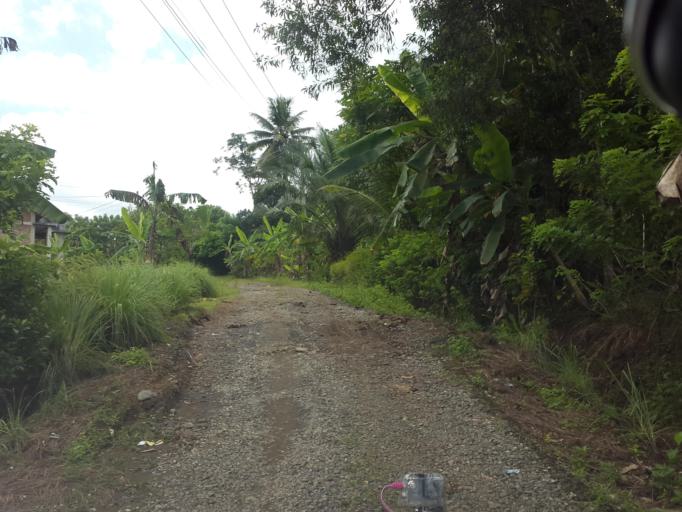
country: ID
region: Central Java
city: Karanglewas
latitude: -7.5677
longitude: 109.1408
